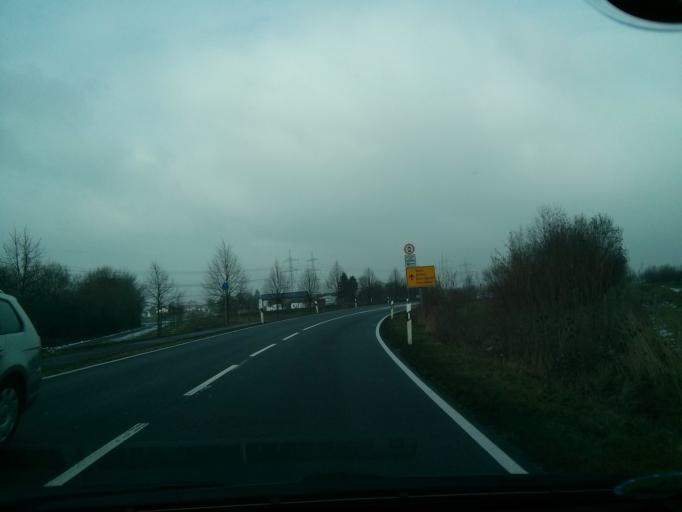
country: DE
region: North Rhine-Westphalia
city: Meckenheim
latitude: 50.6445
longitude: 7.0150
